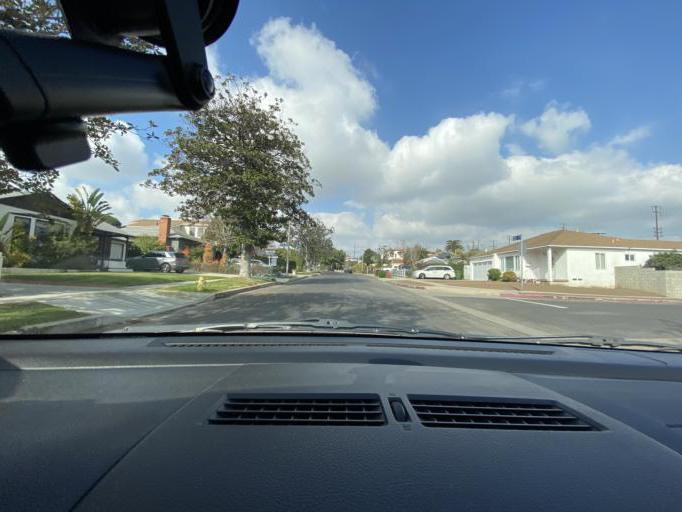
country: US
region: California
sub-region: Los Angeles County
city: Culver City
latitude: 34.0162
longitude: -118.4163
